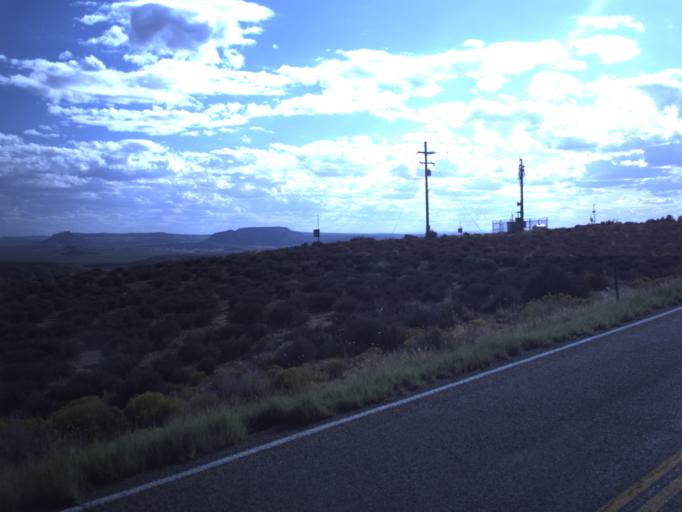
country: US
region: Utah
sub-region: San Juan County
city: Blanding
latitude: 37.3253
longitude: -109.3349
